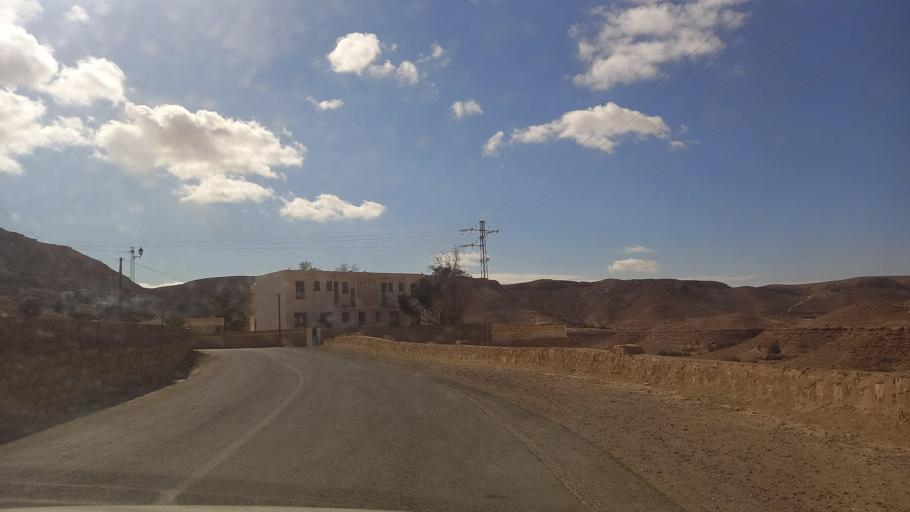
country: TN
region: Tataouine
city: Tataouine
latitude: 32.9114
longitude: 10.2595
